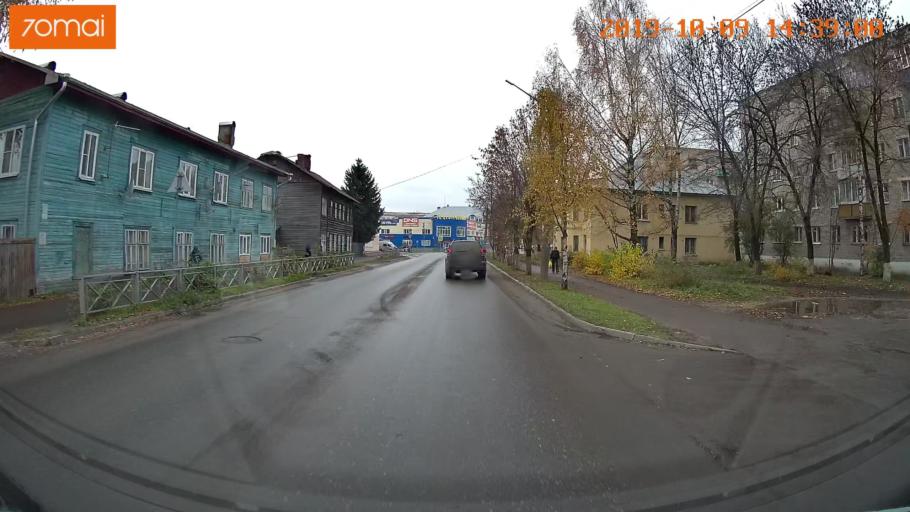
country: RU
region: Kostroma
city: Buy
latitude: 58.4776
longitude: 41.5381
